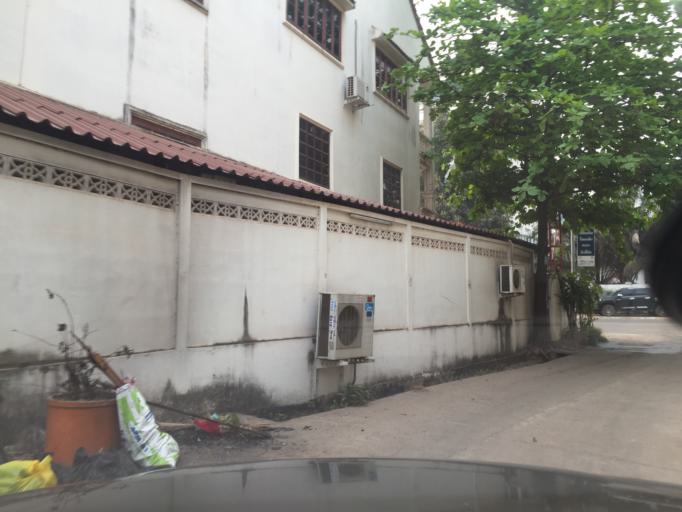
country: LA
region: Vientiane
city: Vientiane
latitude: 17.9733
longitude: 102.6033
